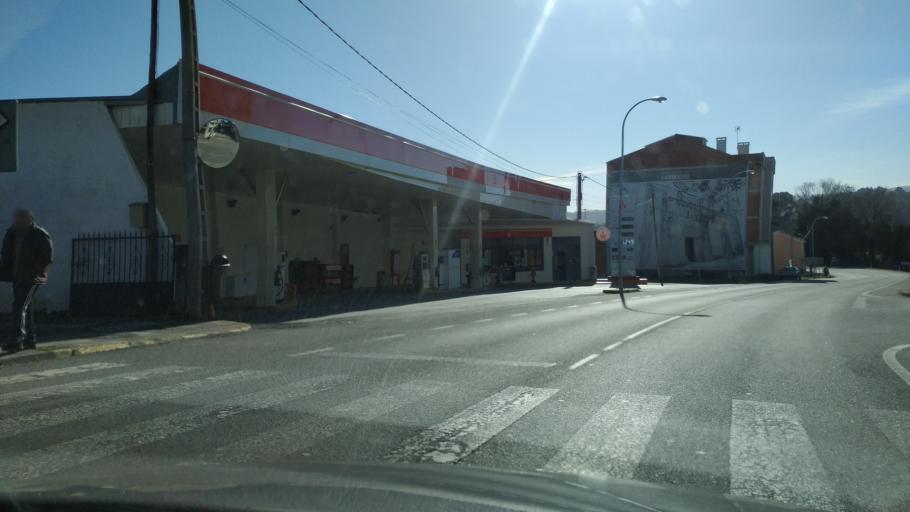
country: ES
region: Galicia
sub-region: Provincia de Pontevedra
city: Silleda
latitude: 42.7286
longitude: -8.3022
